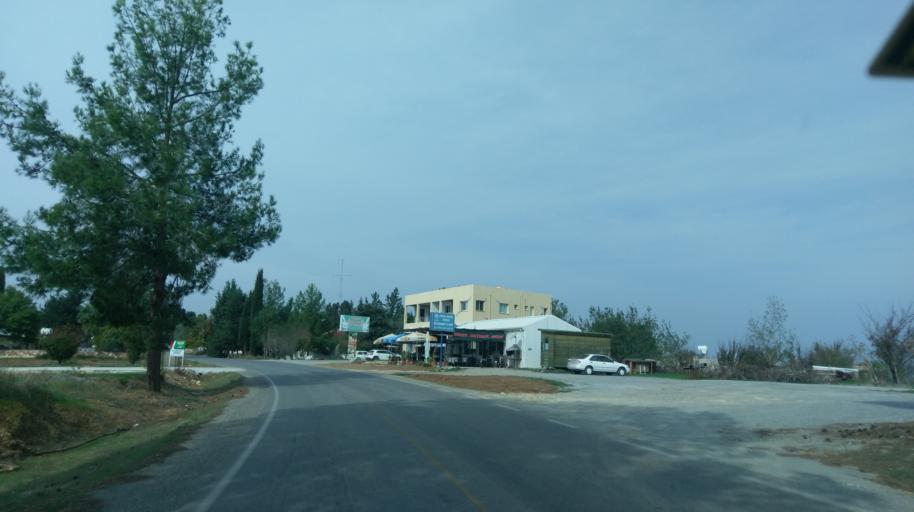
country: CY
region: Keryneia
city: Lapithos
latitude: 35.3140
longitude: 33.0718
